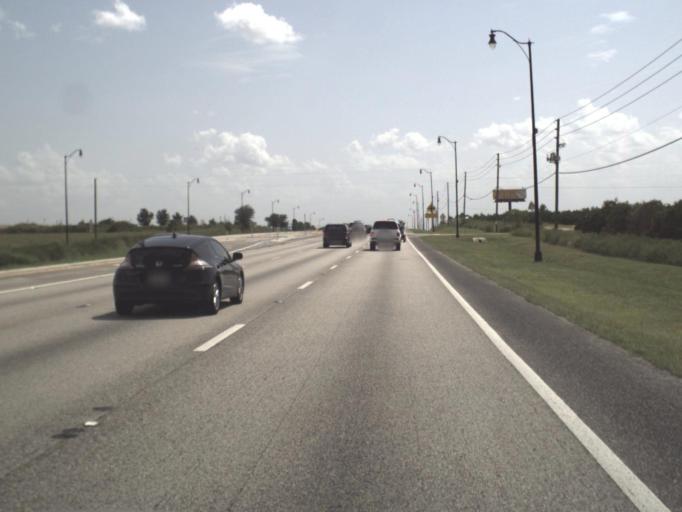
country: US
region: Florida
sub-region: Polk County
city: Davenport
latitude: 28.1698
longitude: -81.6400
